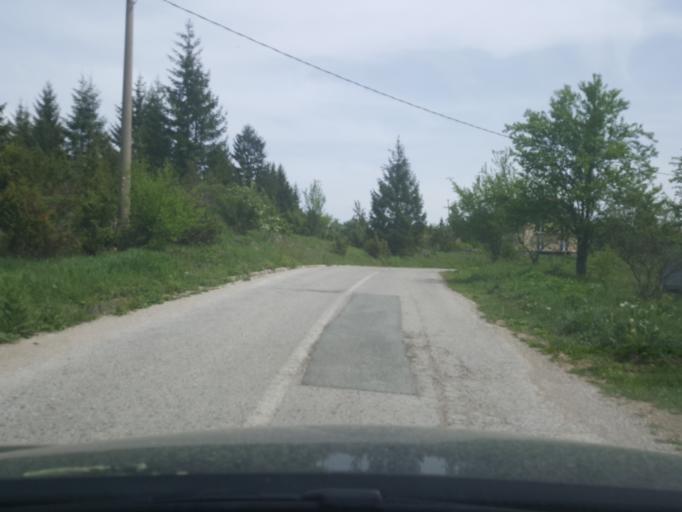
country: RS
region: Central Serbia
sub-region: Zlatiborski Okrug
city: Bajina Basta
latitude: 43.9033
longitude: 19.5100
